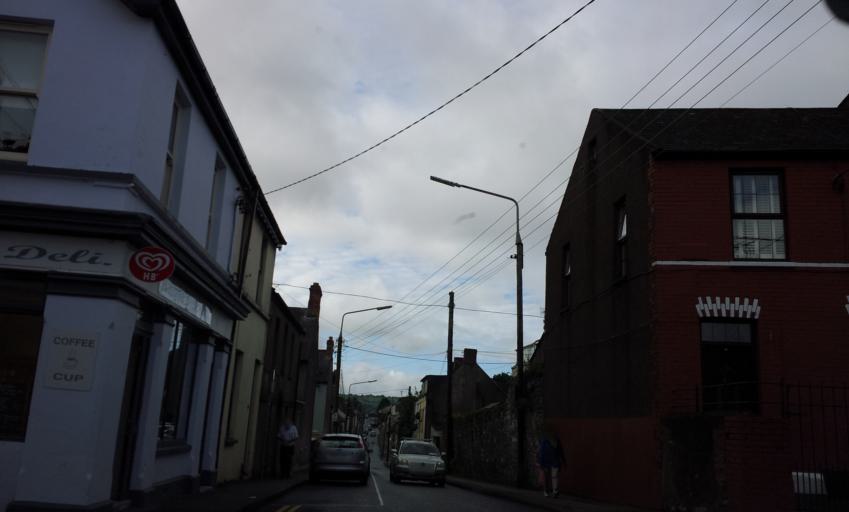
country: IE
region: Munster
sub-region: County Cork
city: Cork
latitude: 51.8922
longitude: -8.4743
